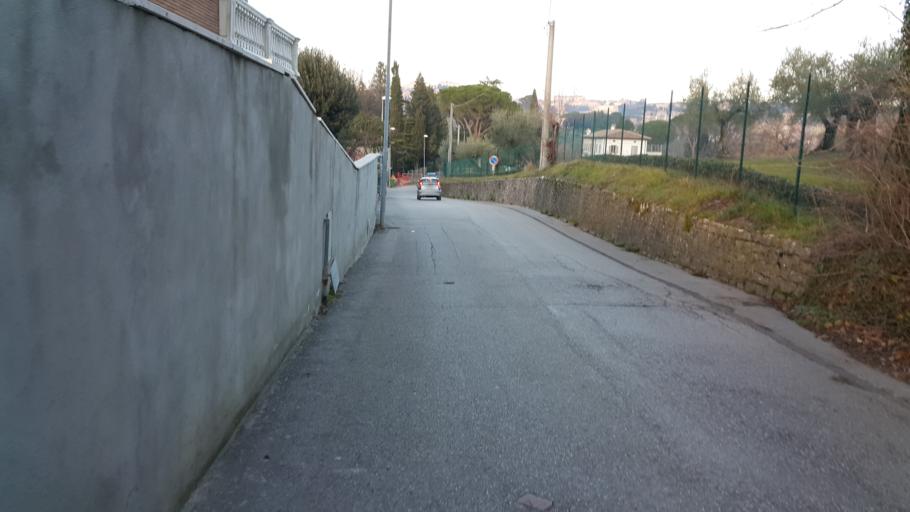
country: IT
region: Umbria
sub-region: Provincia di Perugia
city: Perugia
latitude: 43.0900
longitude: 12.3765
